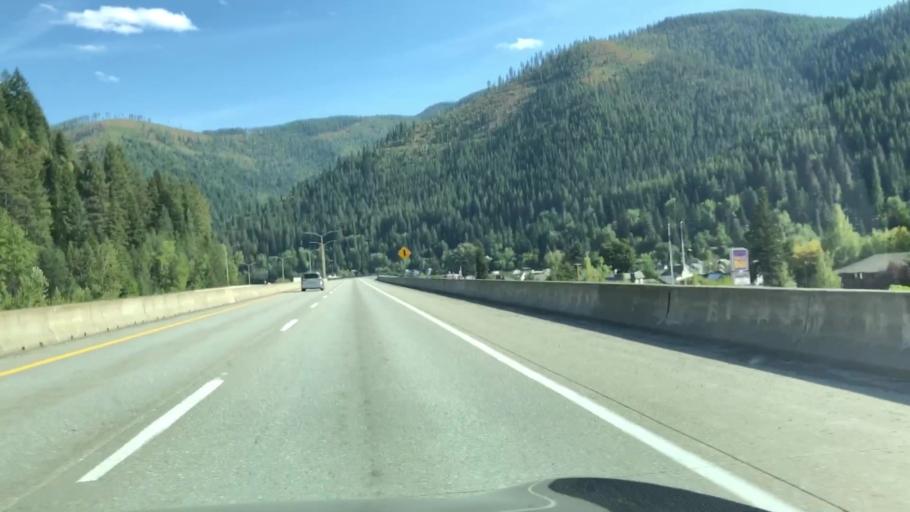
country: US
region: Idaho
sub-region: Shoshone County
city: Wallace
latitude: 47.4773
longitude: -115.9313
